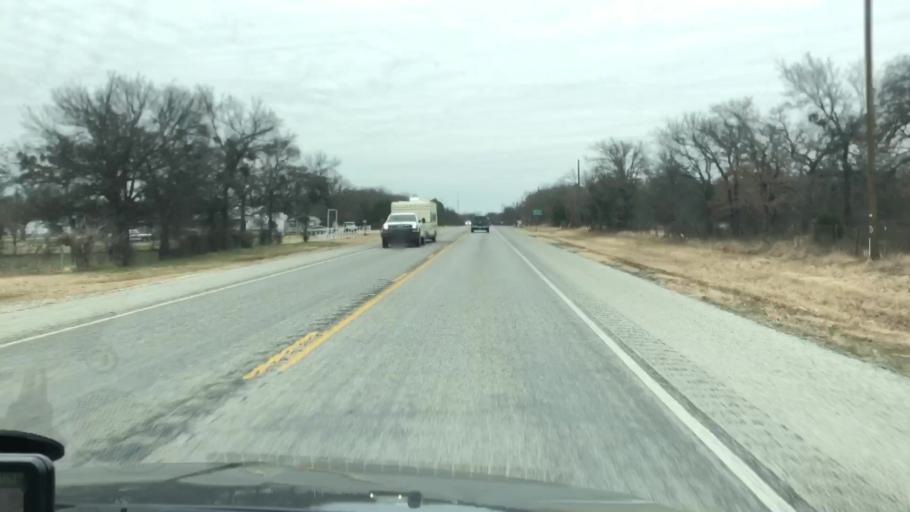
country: US
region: Texas
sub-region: Palo Pinto County
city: Mineral Wells
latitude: 32.8969
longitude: -98.0852
